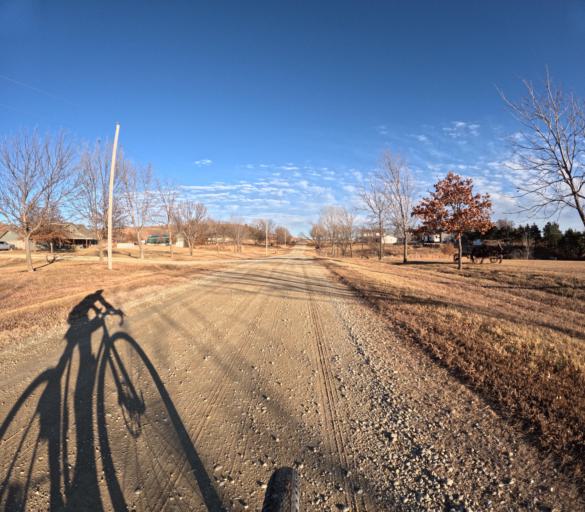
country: US
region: Kansas
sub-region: Riley County
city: Ogden
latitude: 39.2193
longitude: -96.6842
